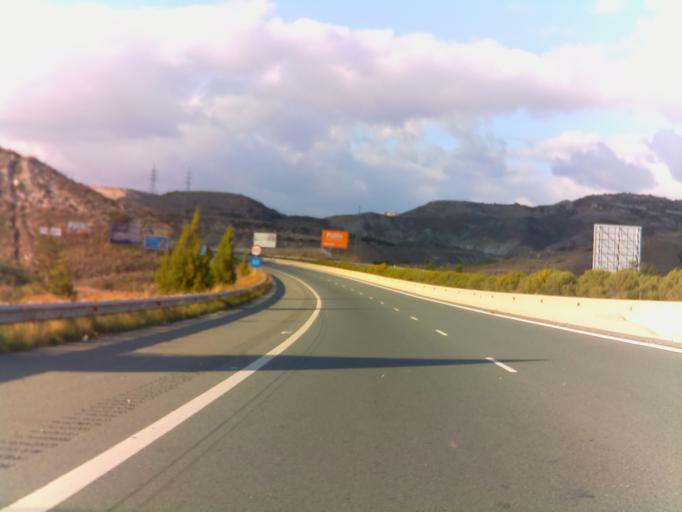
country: CY
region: Pafos
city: Mesogi
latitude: 34.7581
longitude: 32.4915
